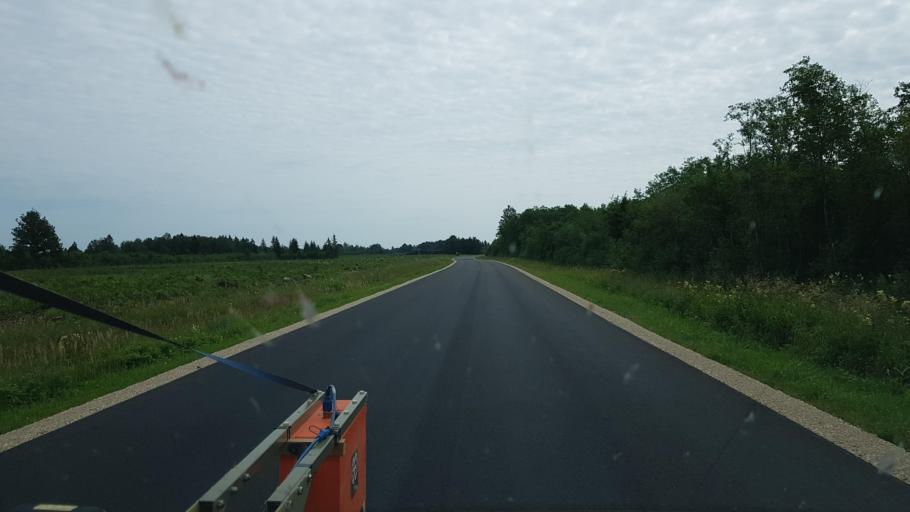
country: EE
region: Paernumaa
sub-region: Halinga vald
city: Parnu-Jaagupi
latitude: 58.6195
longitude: 24.2772
